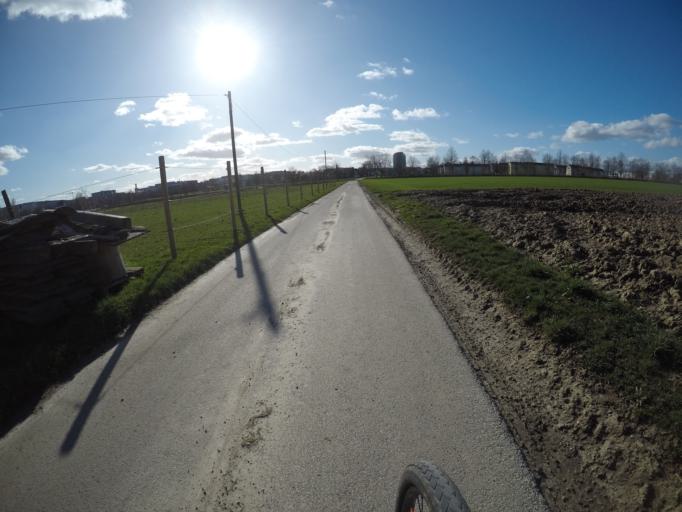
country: DE
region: Baden-Wuerttemberg
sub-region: Regierungsbezirk Stuttgart
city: Leinfelden-Echterdingen
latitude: 48.7038
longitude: 9.1511
